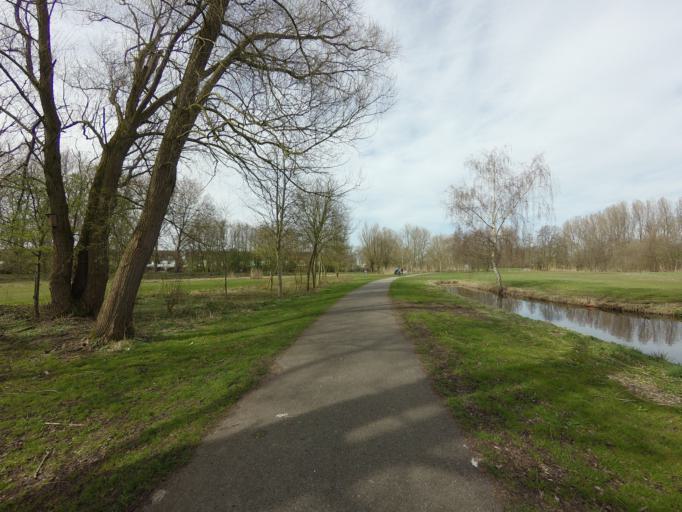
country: NL
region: South Holland
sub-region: Gemeente Alphen aan den Rijn
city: Alphen aan den Rijn
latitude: 52.1485
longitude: 4.6917
